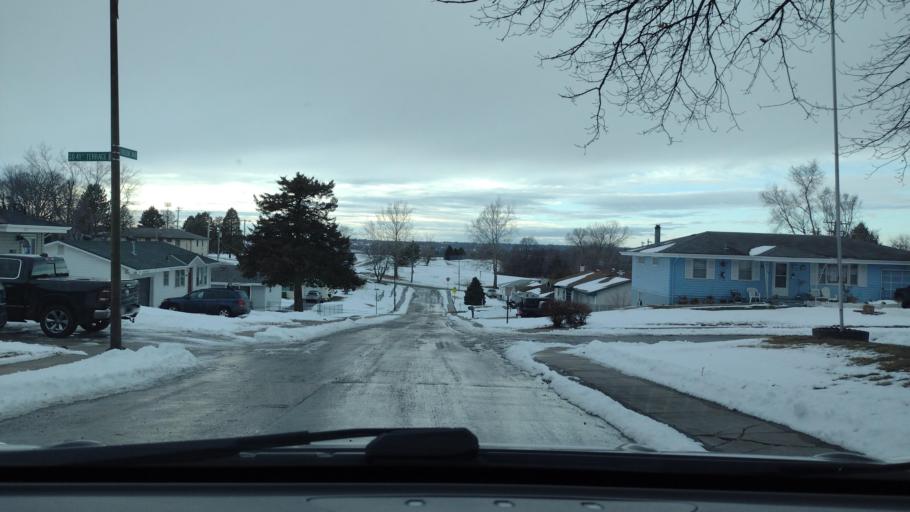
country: US
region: Nebraska
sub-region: Sarpy County
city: La Vista
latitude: 41.1796
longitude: -95.9750
